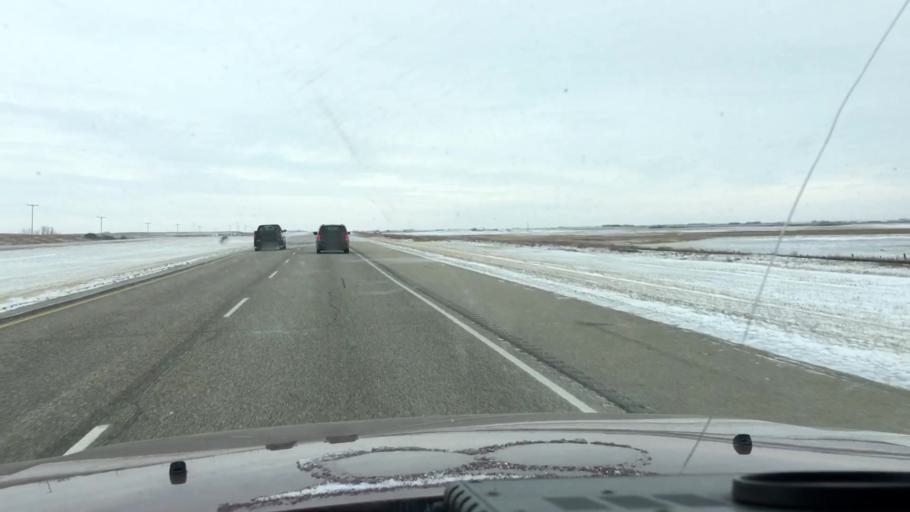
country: CA
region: Saskatchewan
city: Saskatoon
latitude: 51.5980
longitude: -106.3926
